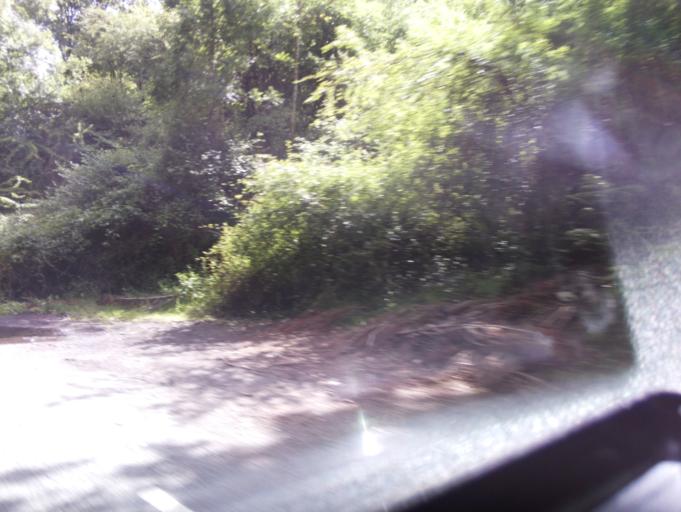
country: GB
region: England
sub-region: Gloucestershire
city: Cinderford
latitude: 51.7769
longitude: -2.5161
